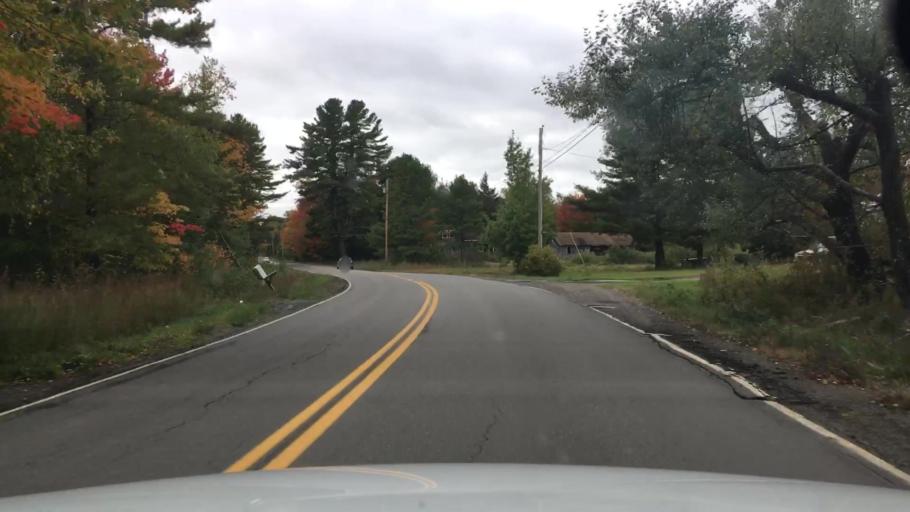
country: US
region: Maine
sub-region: Penobscot County
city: Hudson
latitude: 44.9849
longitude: -68.7802
